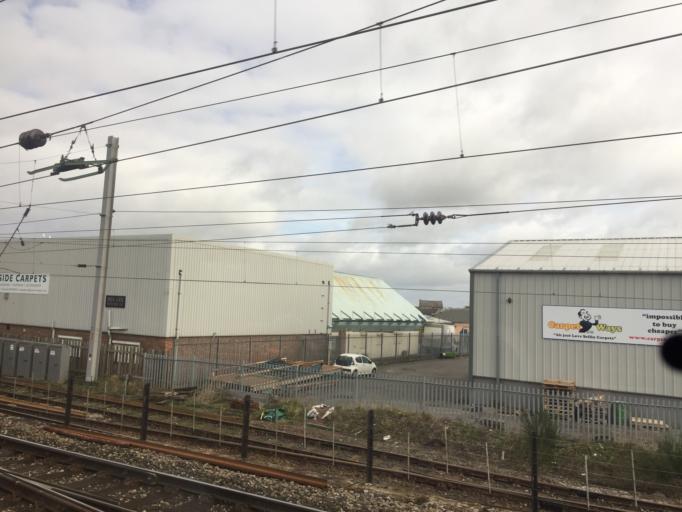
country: GB
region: England
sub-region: Cumbria
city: Carlisle
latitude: 54.8871
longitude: -2.9290
